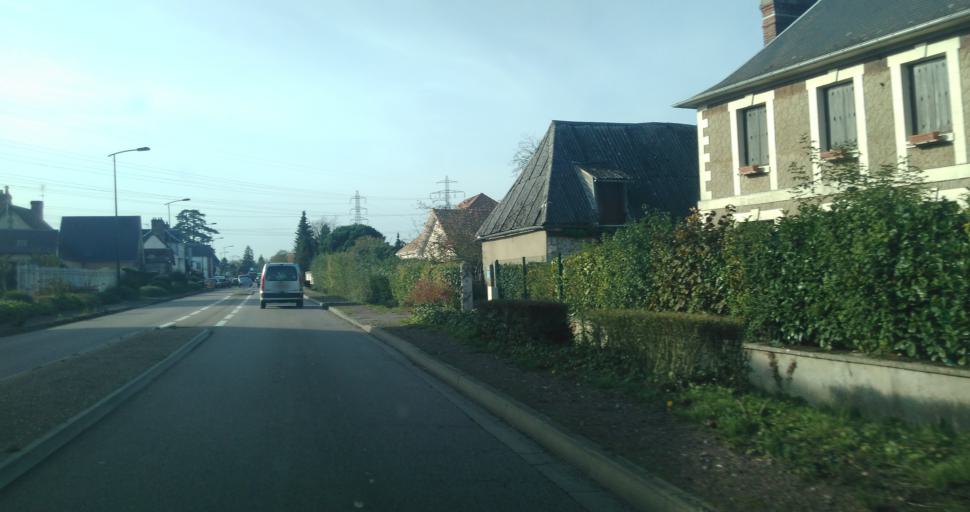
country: FR
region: Haute-Normandie
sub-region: Departement de l'Eure
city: Caumont
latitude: 49.3531
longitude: 0.9141
